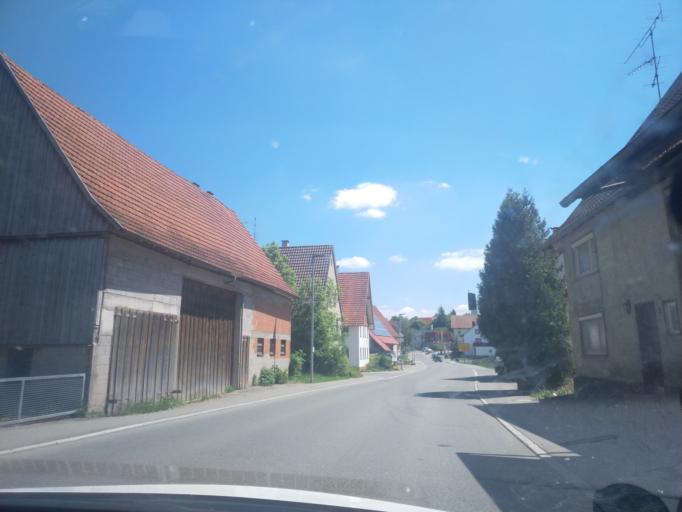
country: DE
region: Baden-Wuerttemberg
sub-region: Freiburg Region
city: Seedorf
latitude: 48.2705
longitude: 8.4839
